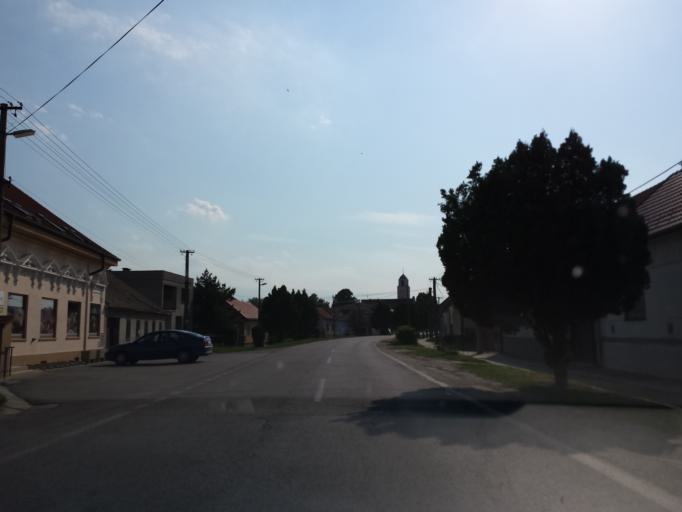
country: AT
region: Lower Austria
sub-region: Politischer Bezirk Ganserndorf
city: Angern an der March
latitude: 48.3824
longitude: 16.8529
